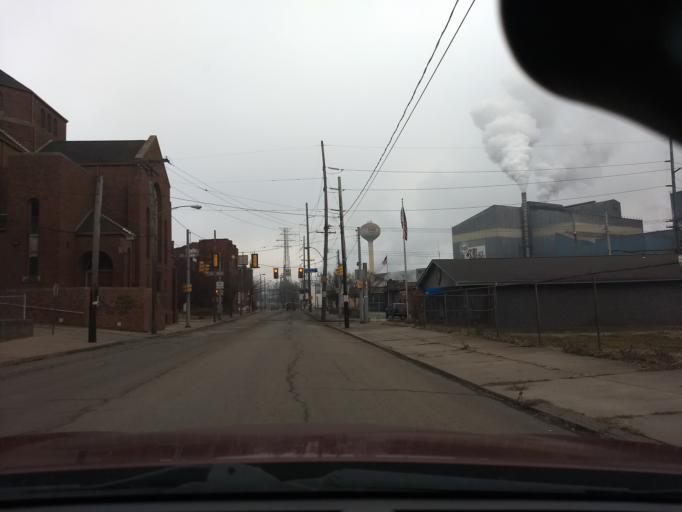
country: US
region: Pennsylvania
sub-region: Allegheny County
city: Braddock
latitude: 40.3988
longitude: -79.8625
